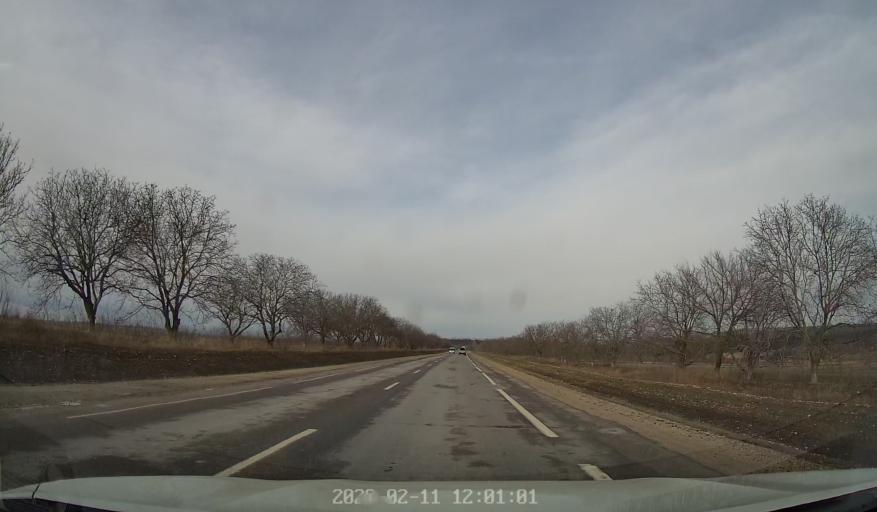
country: MD
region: Riscani
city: Riscani
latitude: 47.9340
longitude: 27.6339
